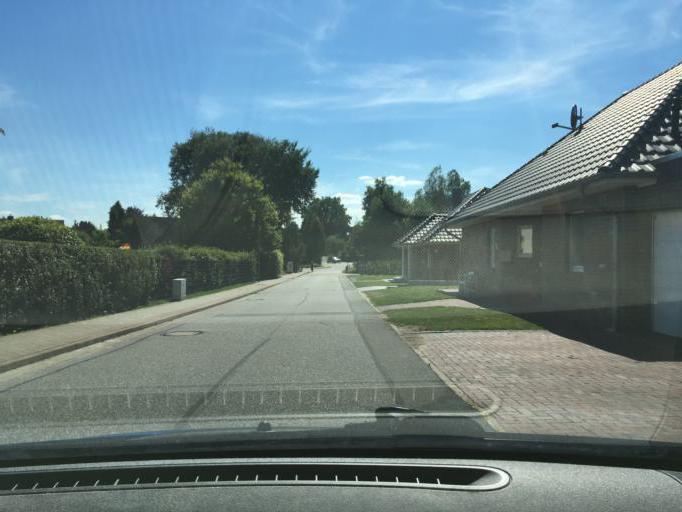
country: DE
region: Lower Saxony
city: Buchholz in der Nordheide
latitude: 53.3790
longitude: 9.8879
